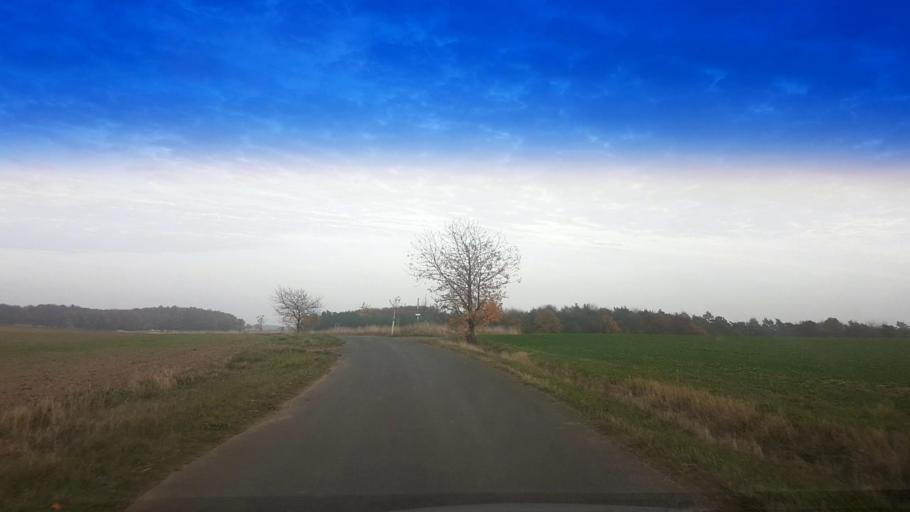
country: DE
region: Bavaria
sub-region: Upper Franconia
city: Priesendorf
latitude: 49.9052
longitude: 10.7363
